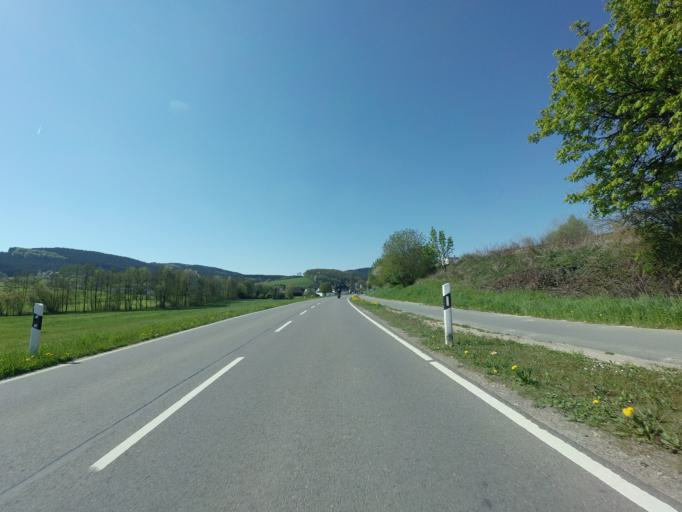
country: DE
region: North Rhine-Westphalia
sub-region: Regierungsbezirk Arnsberg
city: Attendorn
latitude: 51.1090
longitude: 7.9585
